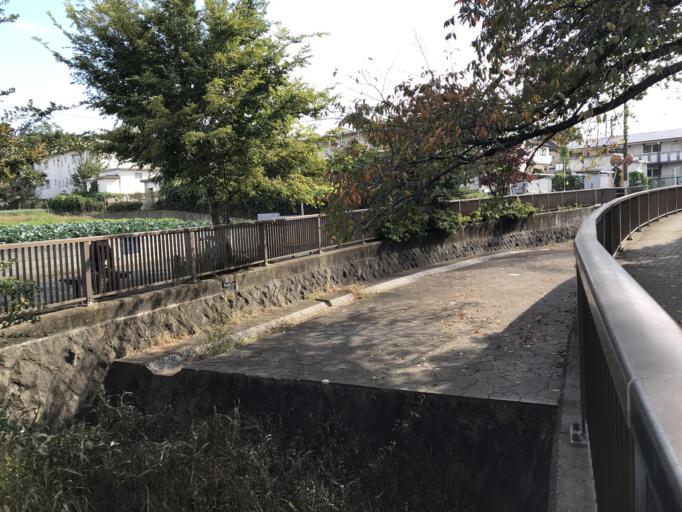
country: JP
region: Tokyo
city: Musashino
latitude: 35.7441
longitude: 139.5769
